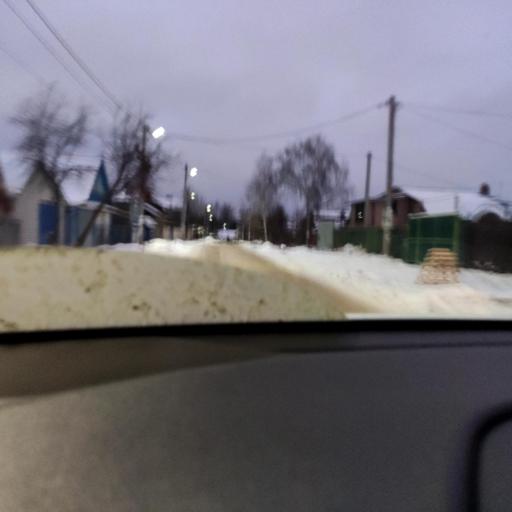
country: RU
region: Tatarstan
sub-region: Gorod Kazan'
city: Kazan
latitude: 55.8785
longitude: 49.0782
